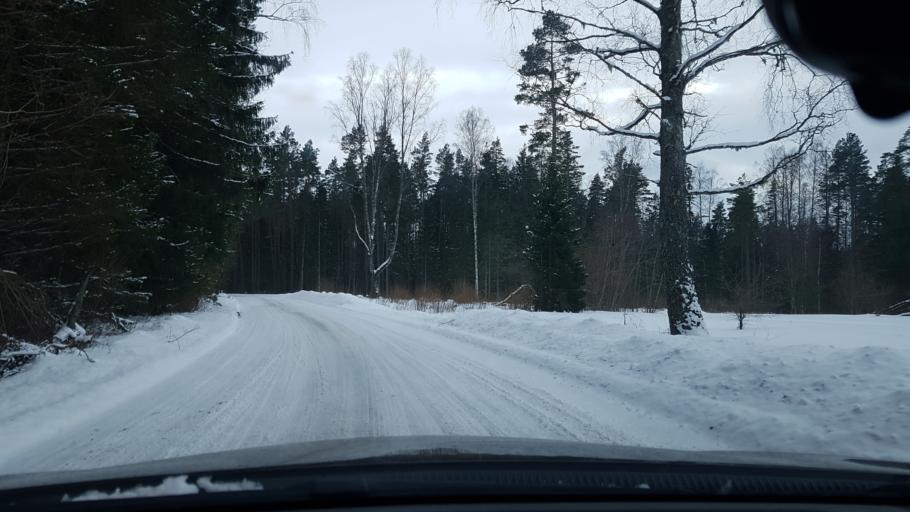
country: EE
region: Laeaene-Virumaa
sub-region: Haljala vald
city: Haljala
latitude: 59.5717
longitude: 26.1170
